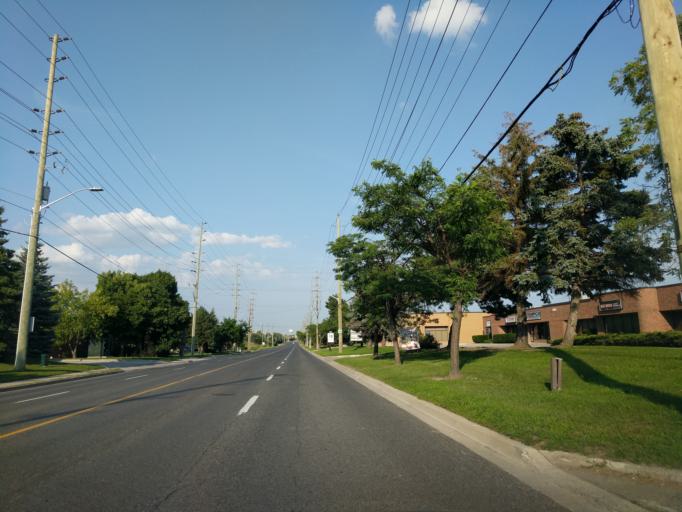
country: CA
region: Ontario
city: Markham
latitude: 43.8340
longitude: -79.3431
